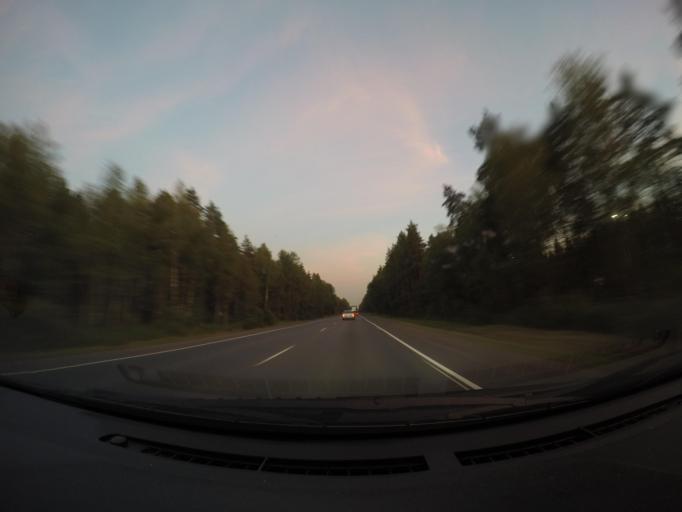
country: RU
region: Moskovskaya
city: Gzhel'
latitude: 55.5537
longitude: 38.3995
